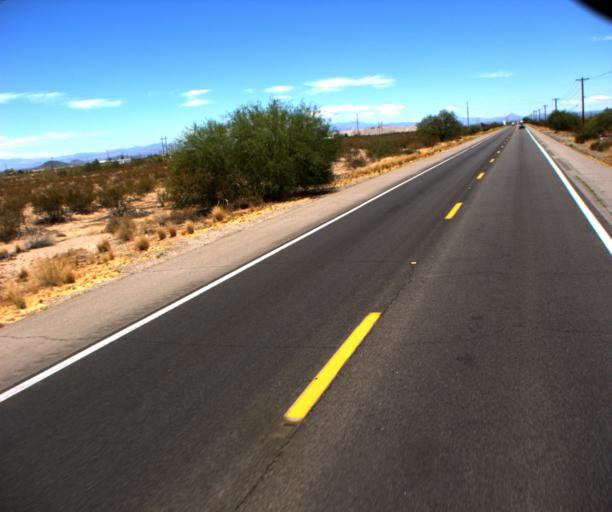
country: US
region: Arizona
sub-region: Pinal County
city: Florence
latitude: 33.0039
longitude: -111.4509
